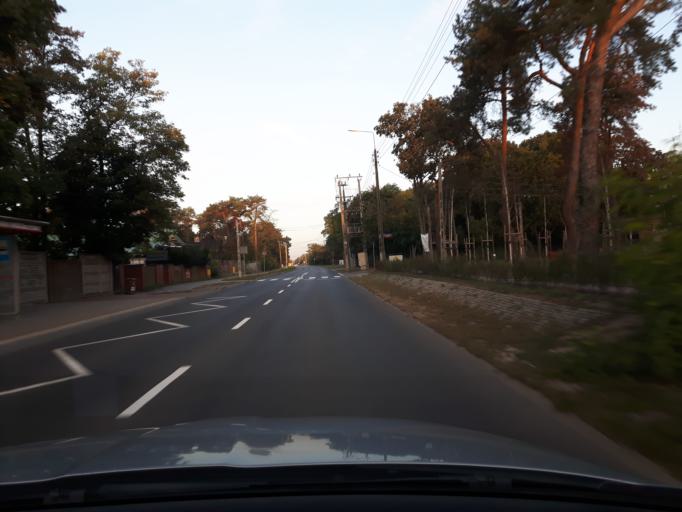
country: PL
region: Masovian Voivodeship
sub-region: Warszawa
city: Wawer
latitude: 52.1841
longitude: 21.1843
